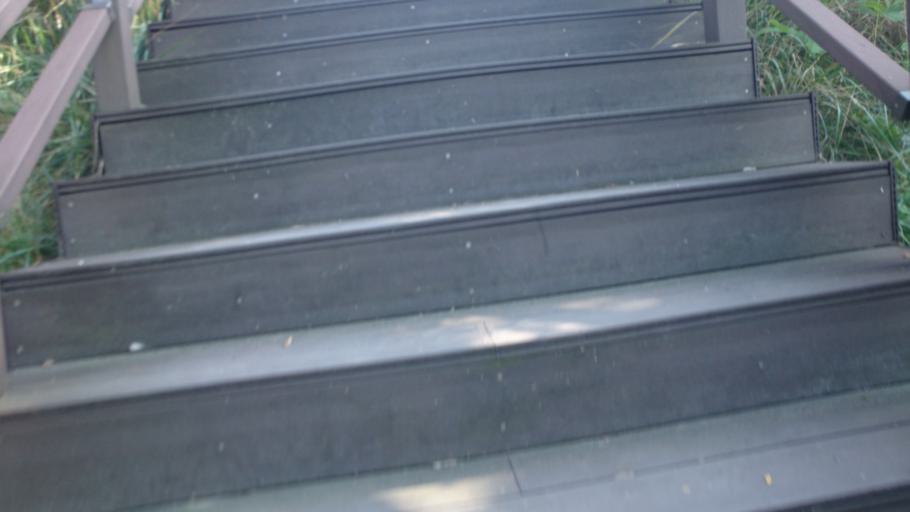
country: KR
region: Gyeongsangbuk-do
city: Gyeongsan-si
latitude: 35.8292
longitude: 128.6747
